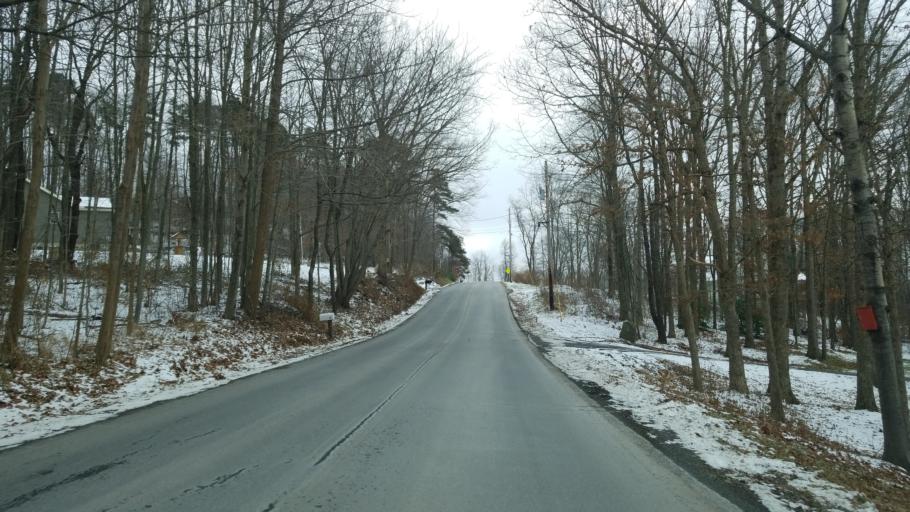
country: US
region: Pennsylvania
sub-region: Clearfield County
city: Sandy
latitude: 41.0959
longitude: -78.7585
